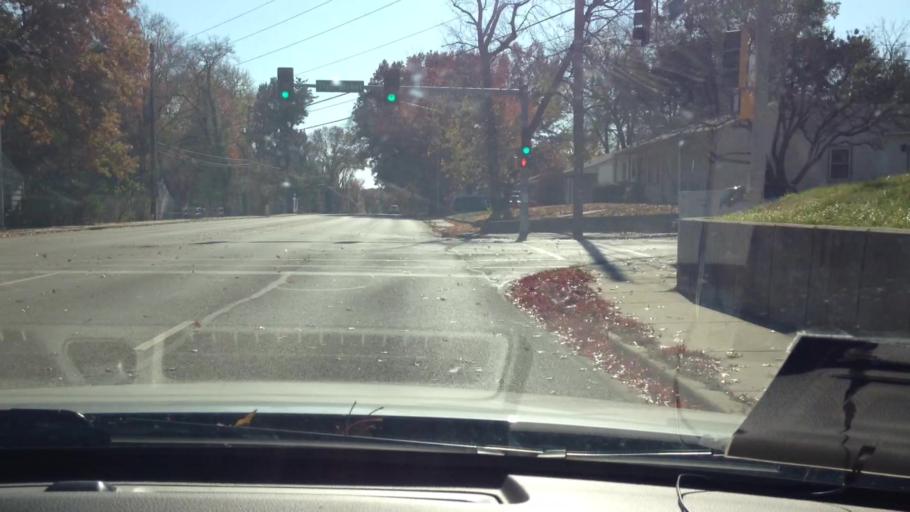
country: US
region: Kansas
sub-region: Johnson County
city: Prairie Village
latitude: 39.0006
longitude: -94.6491
